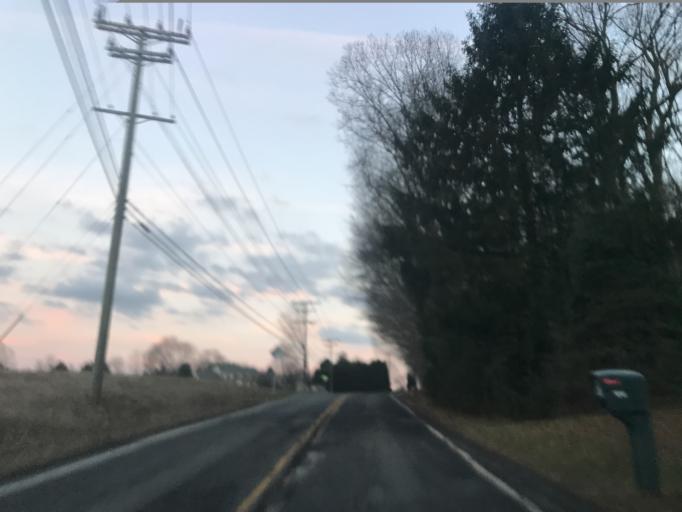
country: US
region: Maryland
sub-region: Harford County
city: Bel Air South
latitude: 39.5344
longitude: -76.2813
